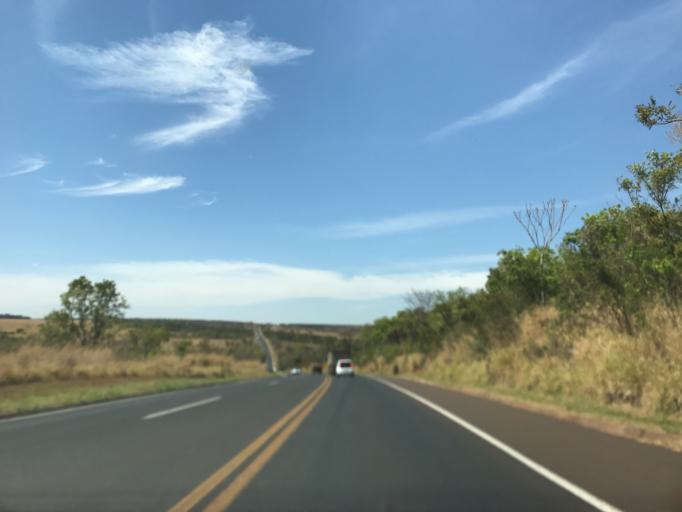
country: BR
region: Minas Gerais
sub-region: Prata
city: Prata
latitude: -19.0829
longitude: -48.9963
